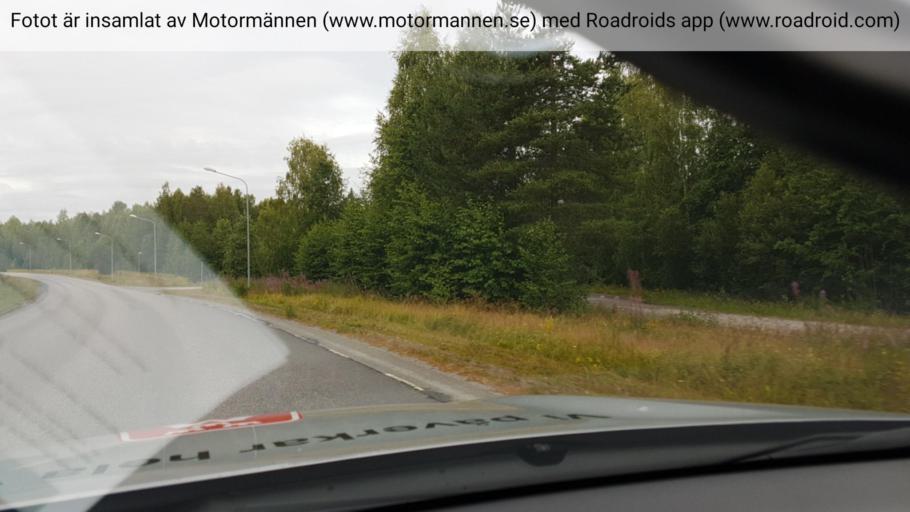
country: SE
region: Norrbotten
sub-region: Bodens Kommun
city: Boden
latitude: 65.8161
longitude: 21.6437
